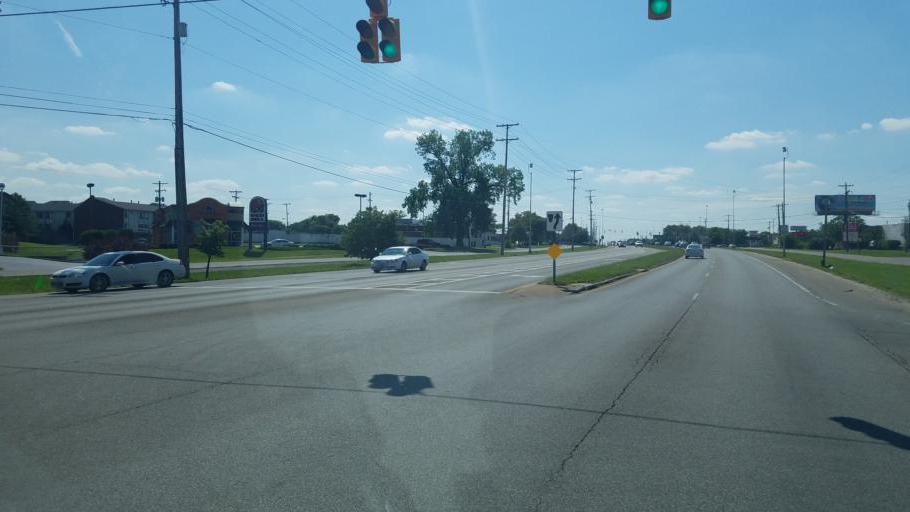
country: US
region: Ohio
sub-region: Franklin County
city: Minerva Park
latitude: 40.0862
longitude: -82.9566
